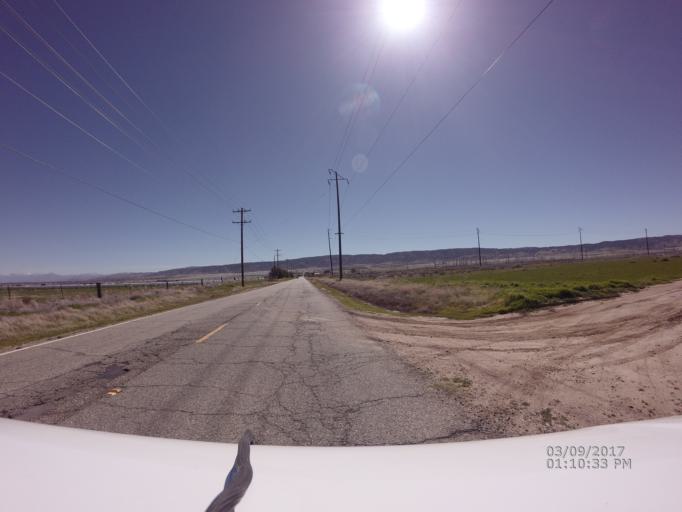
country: US
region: California
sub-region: Los Angeles County
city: Leona Valley
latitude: 34.6974
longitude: -118.2893
